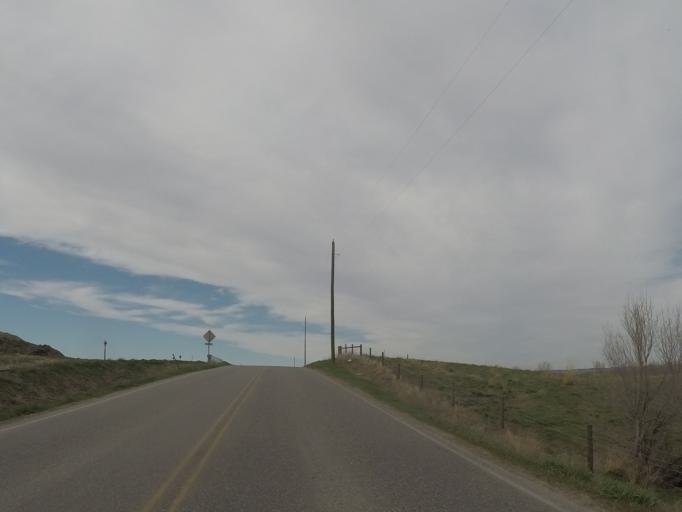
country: US
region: Montana
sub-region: Yellowstone County
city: Laurel
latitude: 45.7125
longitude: -108.6587
